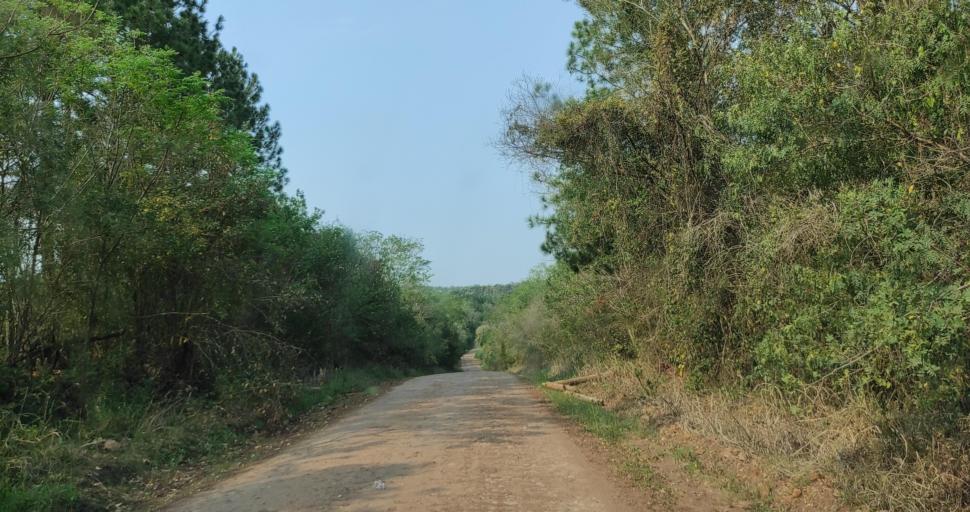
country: AR
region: Misiones
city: Cerro Azul
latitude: -27.6263
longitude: -55.5405
